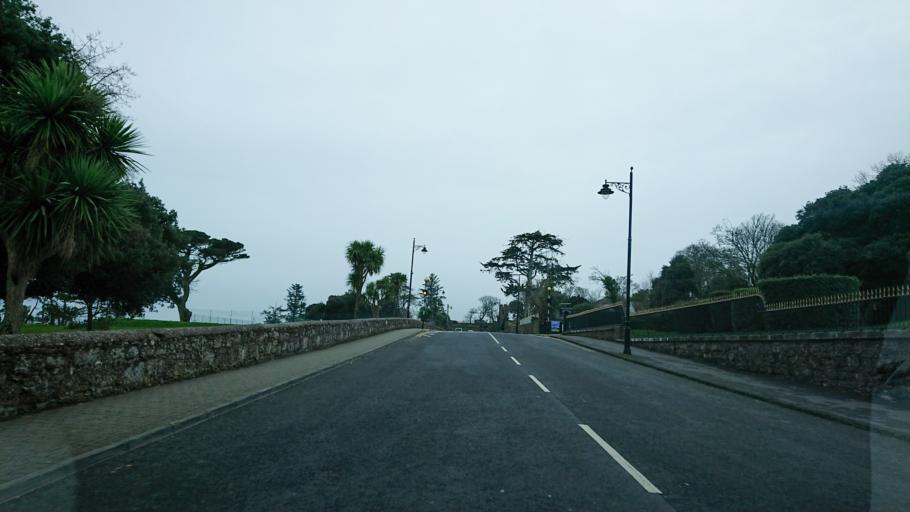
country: IE
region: Munster
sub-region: Waterford
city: Dunmore East
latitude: 52.1524
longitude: -6.9947
